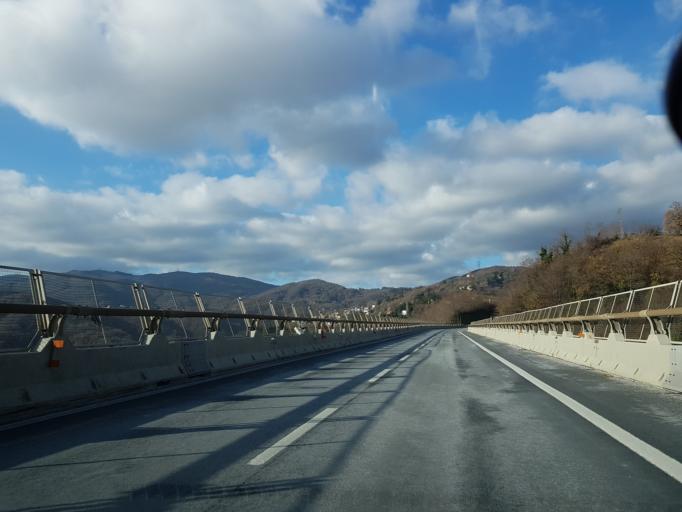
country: IT
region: Liguria
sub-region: Provincia di Genova
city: Serra Ricco
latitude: 44.5393
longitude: 8.9422
